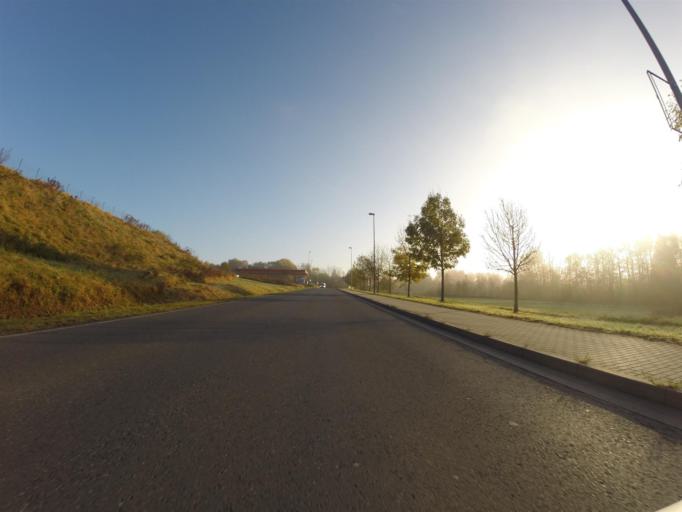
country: DE
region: Thuringia
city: Eisenberg
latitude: 50.9798
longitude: 11.8949
